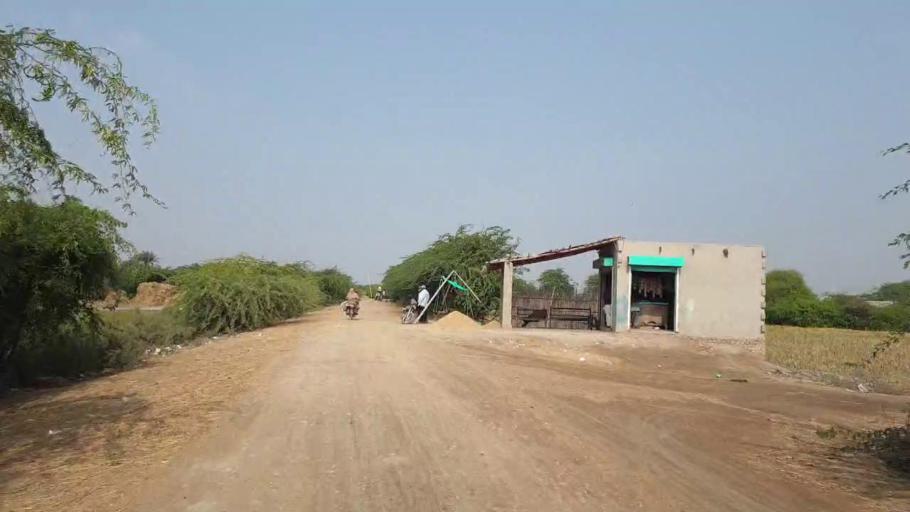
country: PK
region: Sindh
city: Kario
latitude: 24.7561
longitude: 68.5584
